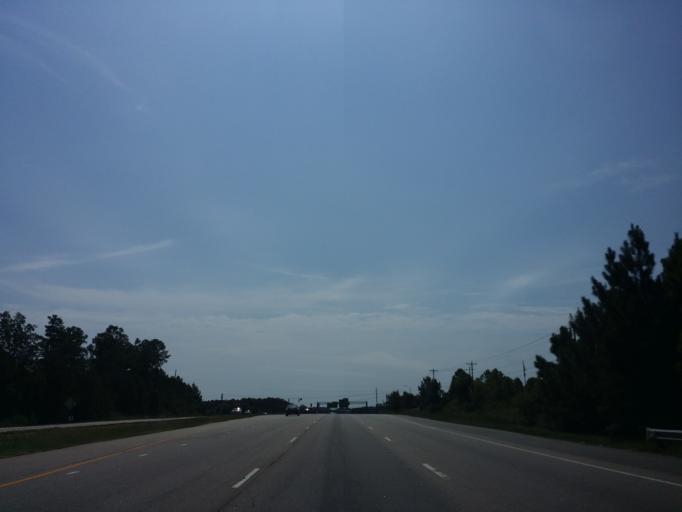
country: US
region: North Carolina
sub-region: Wake County
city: Morrisville
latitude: 35.9139
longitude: -78.7843
